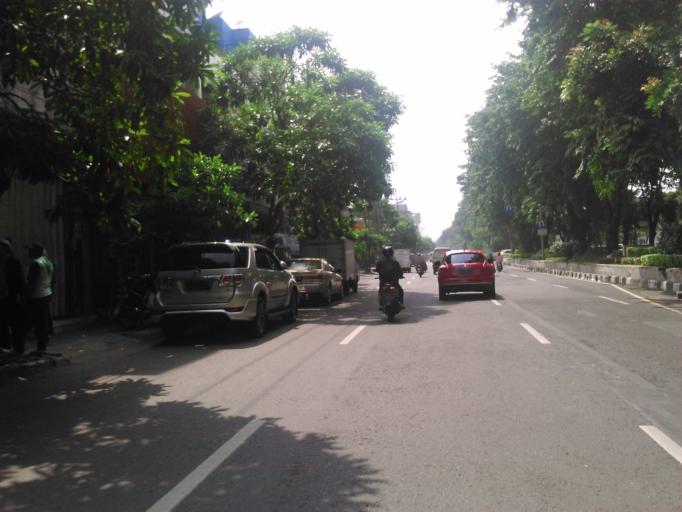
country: ID
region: East Java
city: Gubengairlangga
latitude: -7.2777
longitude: 112.7531
